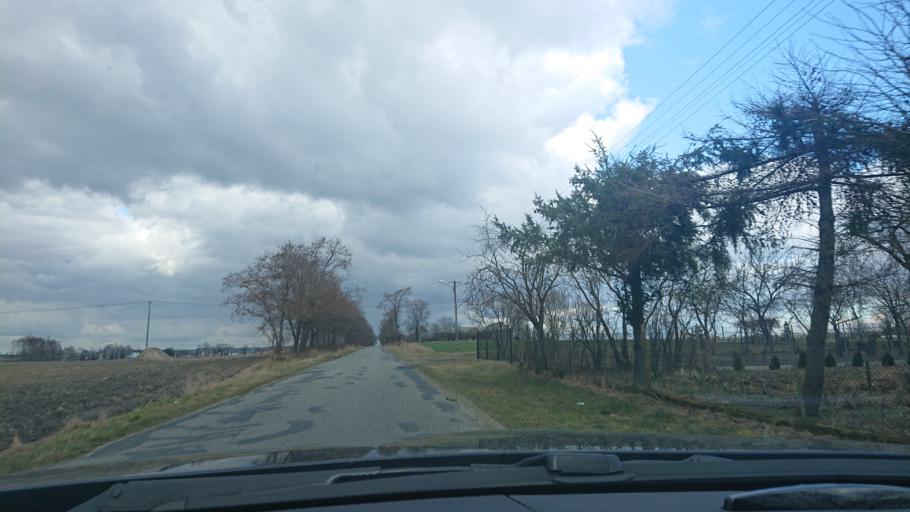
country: PL
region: Greater Poland Voivodeship
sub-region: Powiat gnieznienski
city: Niechanowo
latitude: 52.5695
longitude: 17.7028
